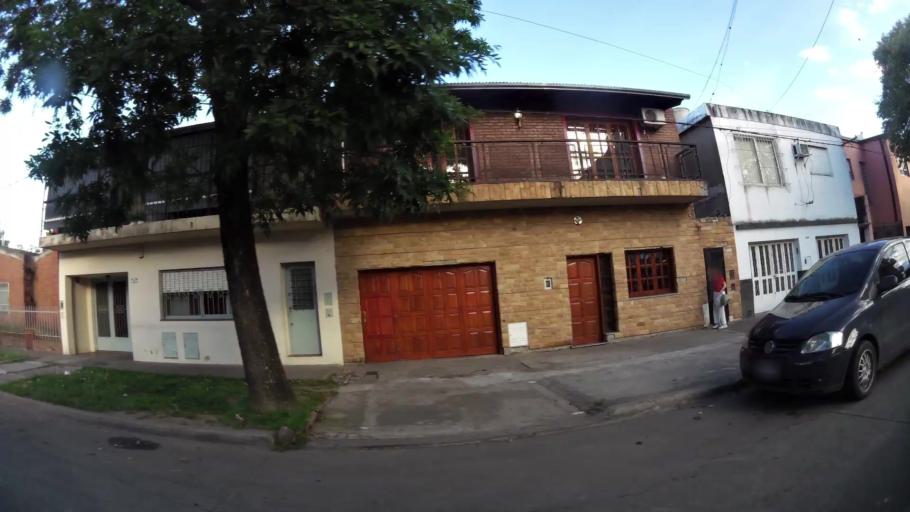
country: AR
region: Santa Fe
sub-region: Departamento de Rosario
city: Rosario
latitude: -32.9766
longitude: -60.6630
